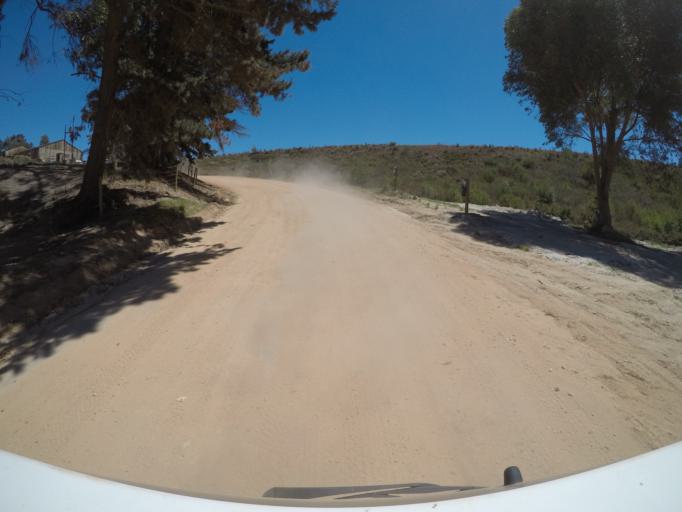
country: ZA
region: Western Cape
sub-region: Overberg District Municipality
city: Grabouw
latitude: -34.2432
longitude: 19.0953
